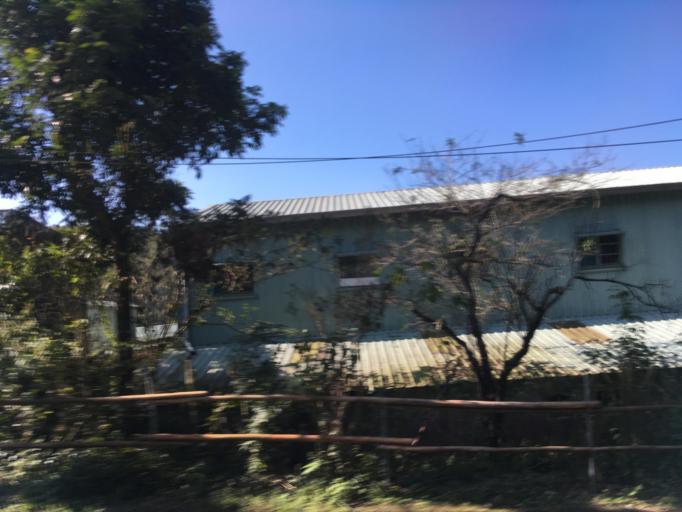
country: TW
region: Taiwan
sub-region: Chiayi
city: Jiayi Shi
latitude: 23.4198
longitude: 120.6436
